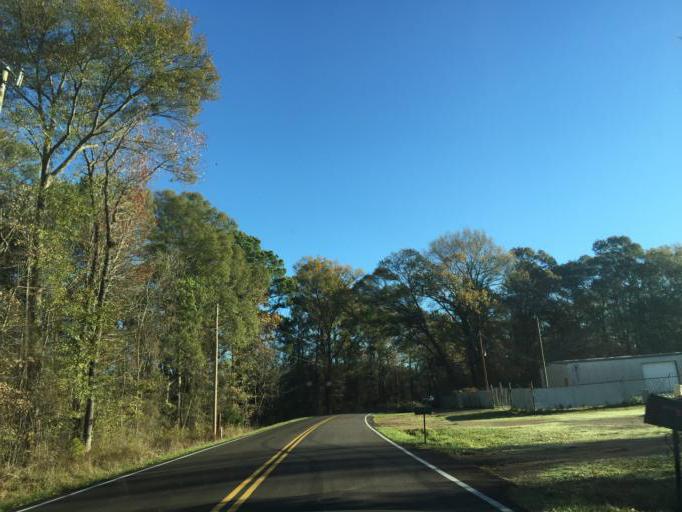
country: US
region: Mississippi
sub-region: Hinds County
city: Jackson
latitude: 32.2848
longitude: -90.1602
